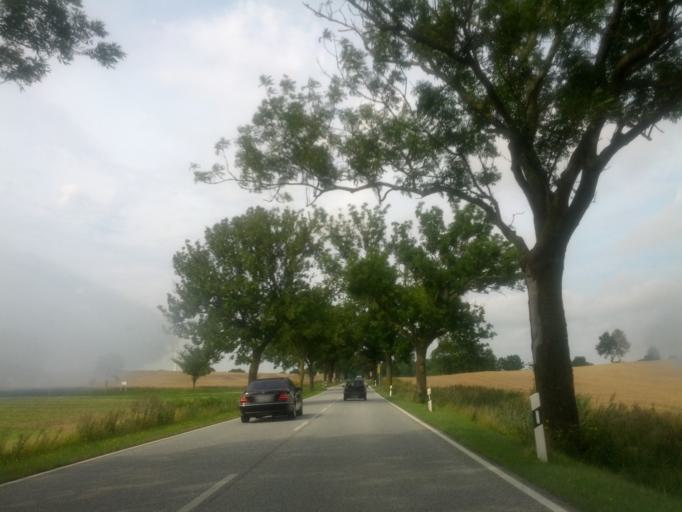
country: DE
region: Mecklenburg-Vorpommern
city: Neubukow
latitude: 53.9774
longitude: 11.6249
